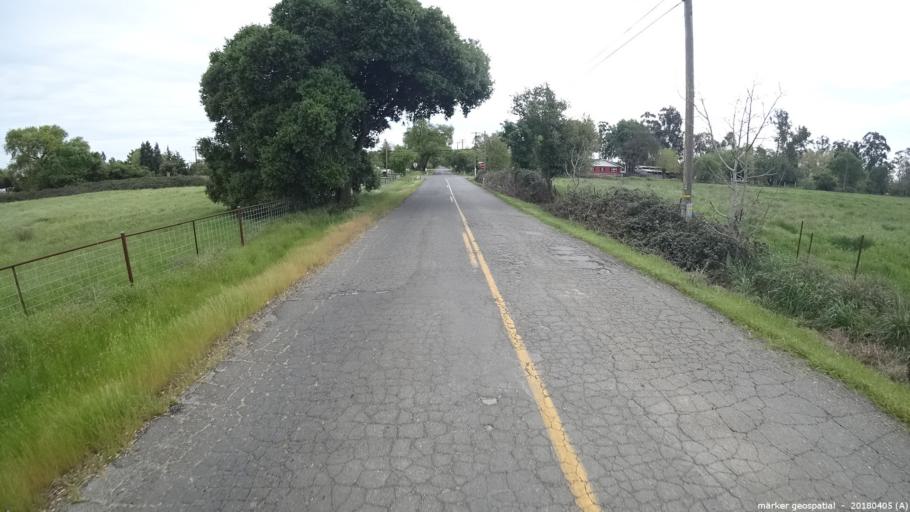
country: US
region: California
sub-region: Sacramento County
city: Galt
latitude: 38.2546
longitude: -121.3382
